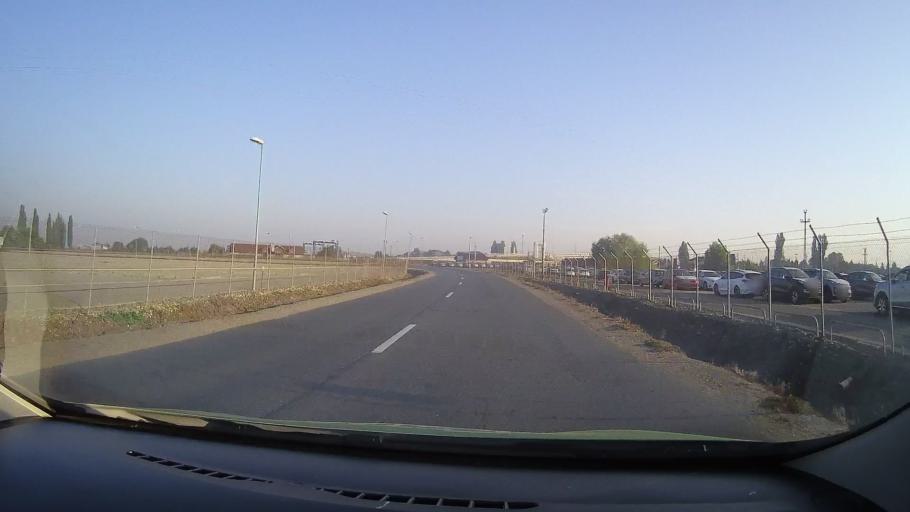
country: RO
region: Arad
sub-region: Comuna Curtici
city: Curtici
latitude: 46.3347
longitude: 21.2975
